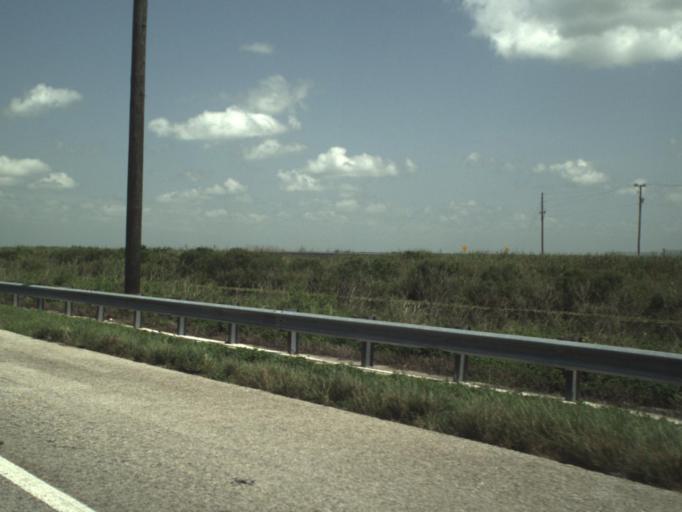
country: US
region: Florida
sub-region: Palm Beach County
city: Belle Glade Camp
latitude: 26.4321
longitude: -80.6128
